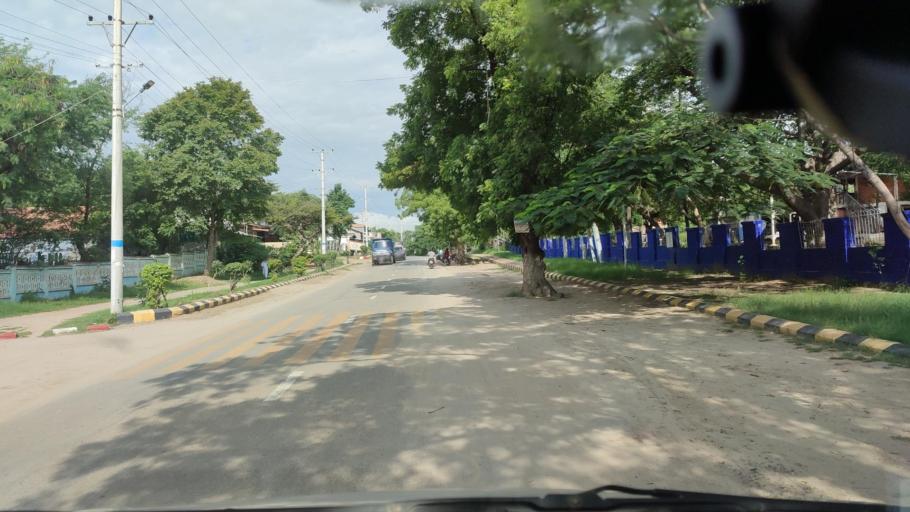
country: MM
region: Mandalay
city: Meiktila
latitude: 21.1003
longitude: 95.6490
